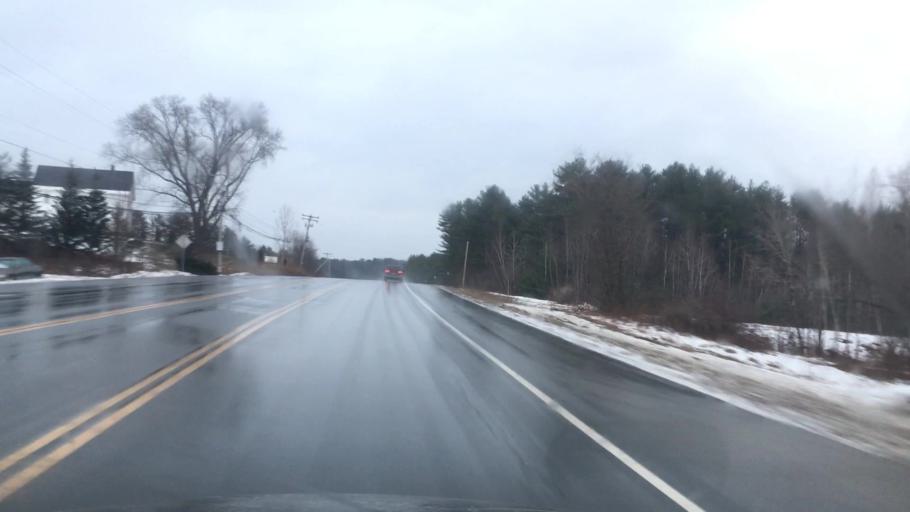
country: US
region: New Hampshire
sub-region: Sullivan County
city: Newport
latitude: 43.3652
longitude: -72.2360
